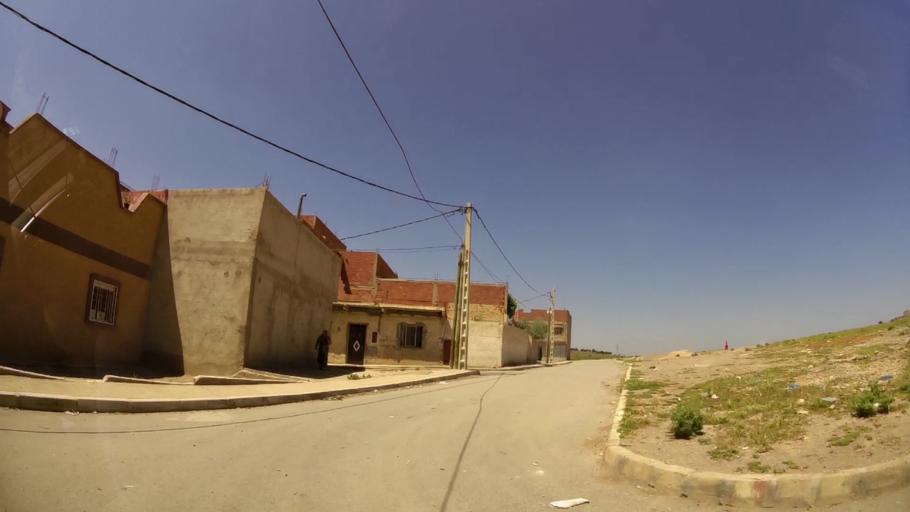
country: MA
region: Oriental
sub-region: Oujda-Angad
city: Oujda
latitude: 34.6810
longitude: -1.9583
